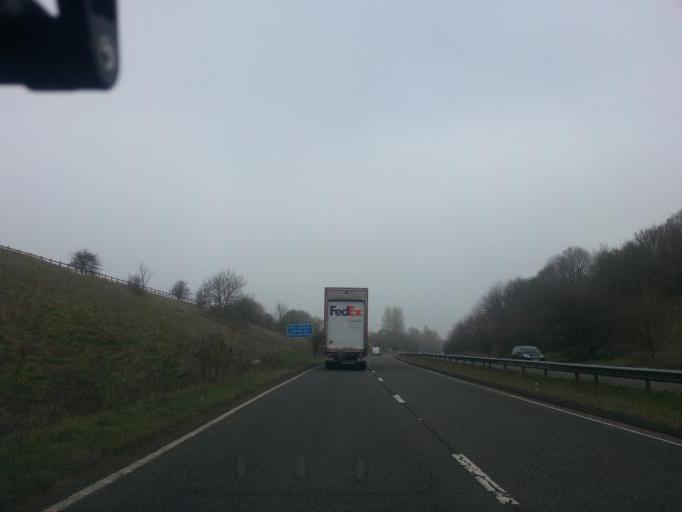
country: GB
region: England
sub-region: Oxfordshire
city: Boars Hill
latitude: 51.7367
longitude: -1.3276
